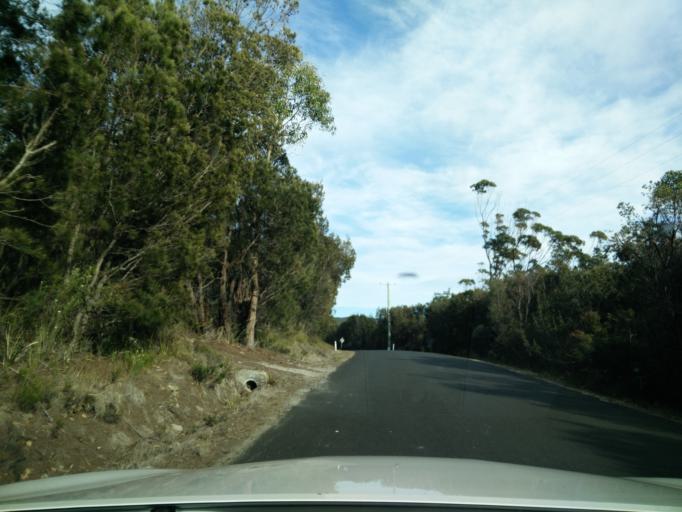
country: AU
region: Tasmania
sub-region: Break O'Day
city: St Helens
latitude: -41.8542
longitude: 148.2648
